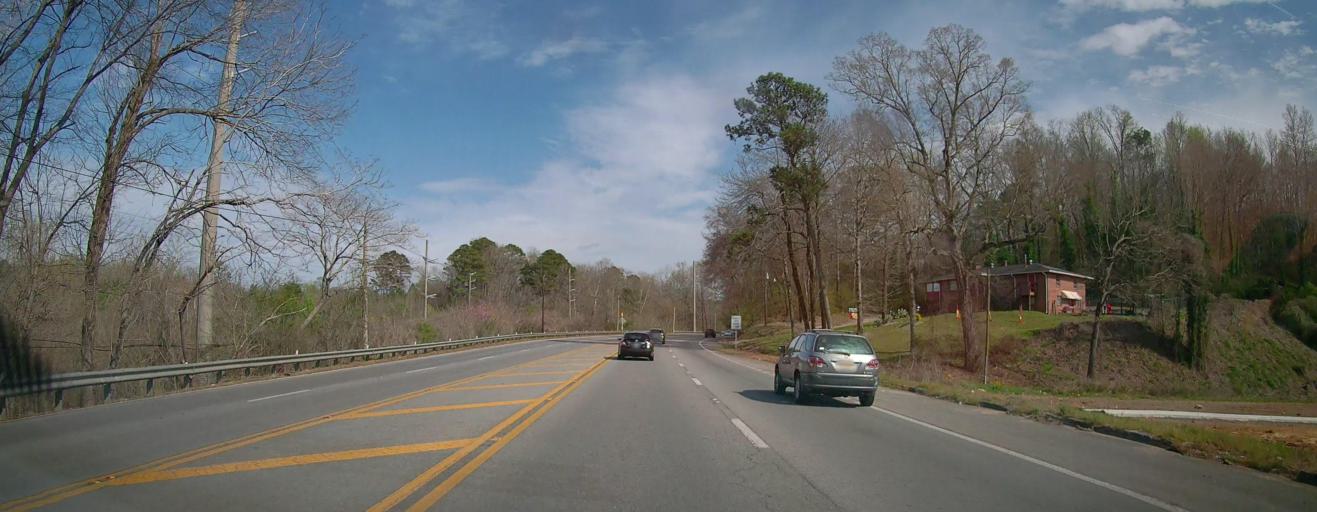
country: US
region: Alabama
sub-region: Jefferson County
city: Forestdale
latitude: 33.5736
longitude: -86.9047
